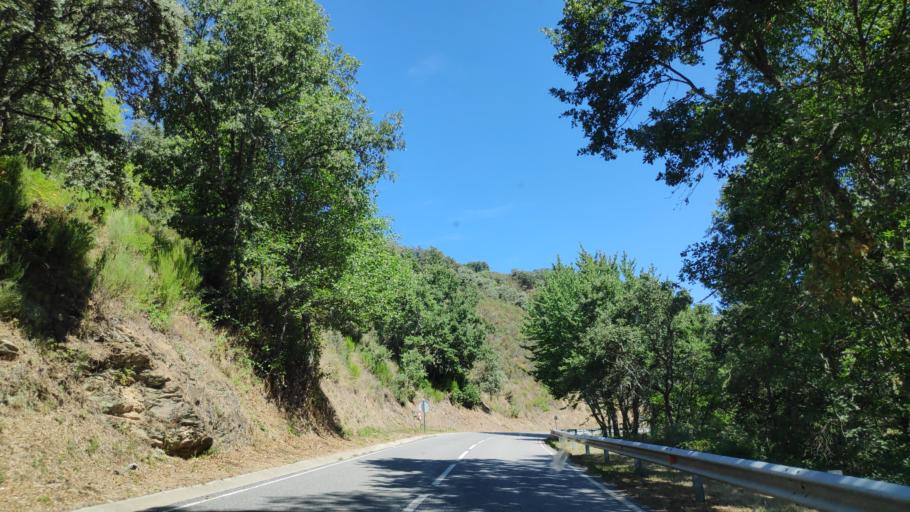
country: PT
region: Braganca
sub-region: Braganca Municipality
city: Braganca
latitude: 41.8916
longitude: -6.7306
